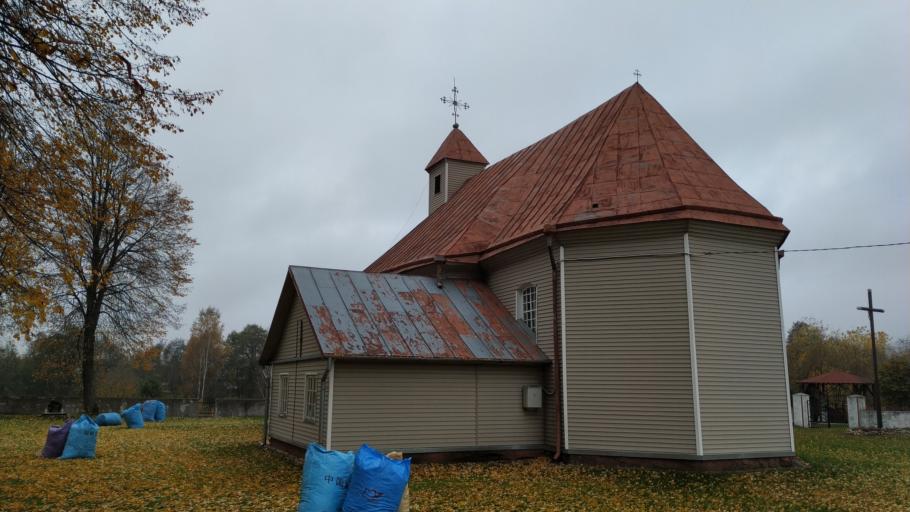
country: LT
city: Skaidiskes
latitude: 54.6478
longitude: 25.6232
